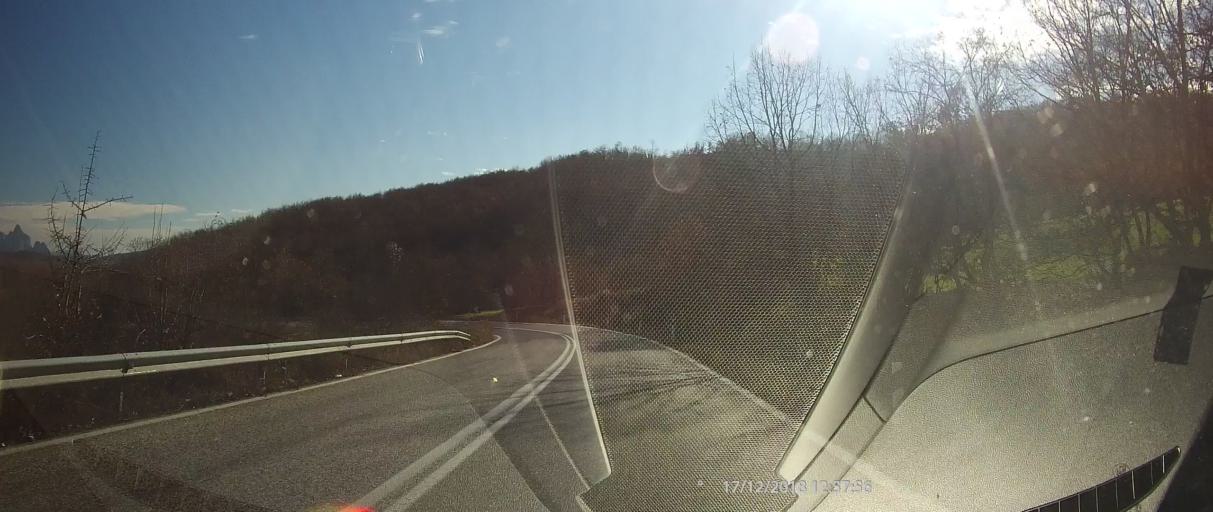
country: GR
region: Thessaly
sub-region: Trikala
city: Kastraki
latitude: 39.7430
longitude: 21.5360
